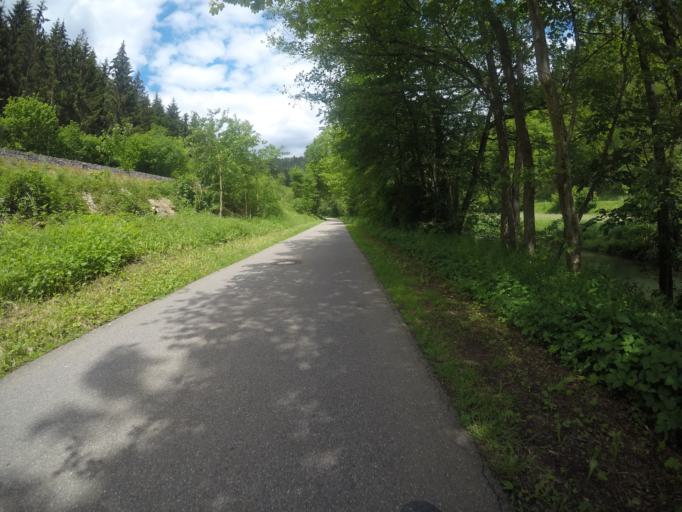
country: DE
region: Baden-Wuerttemberg
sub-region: Karlsruhe Region
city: Wildberg
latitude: 48.6388
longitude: 8.7450
